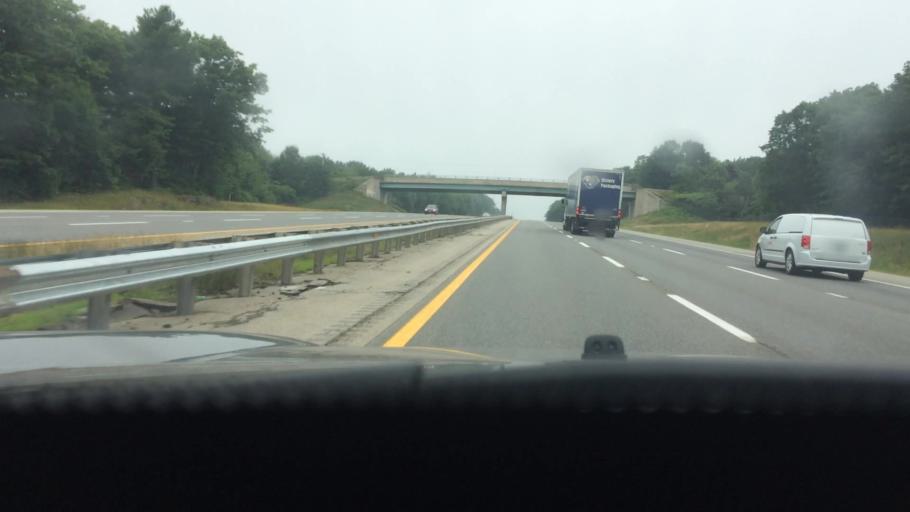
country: US
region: Maine
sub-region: York County
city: Ogunquit
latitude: 43.2702
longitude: -70.6186
